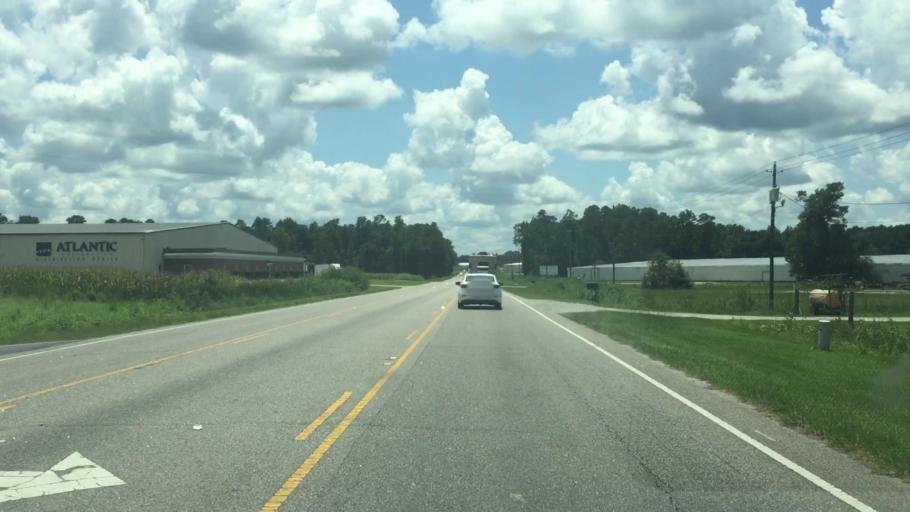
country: US
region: North Carolina
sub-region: Columbus County
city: Tabor City
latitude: 34.1522
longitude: -78.8605
